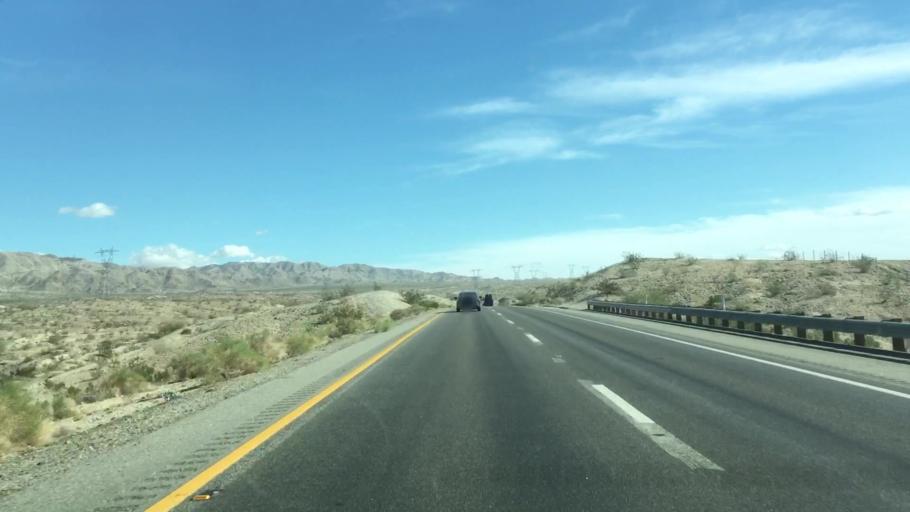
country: US
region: California
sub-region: Riverside County
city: Thermal
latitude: 33.6998
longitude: -116.0730
